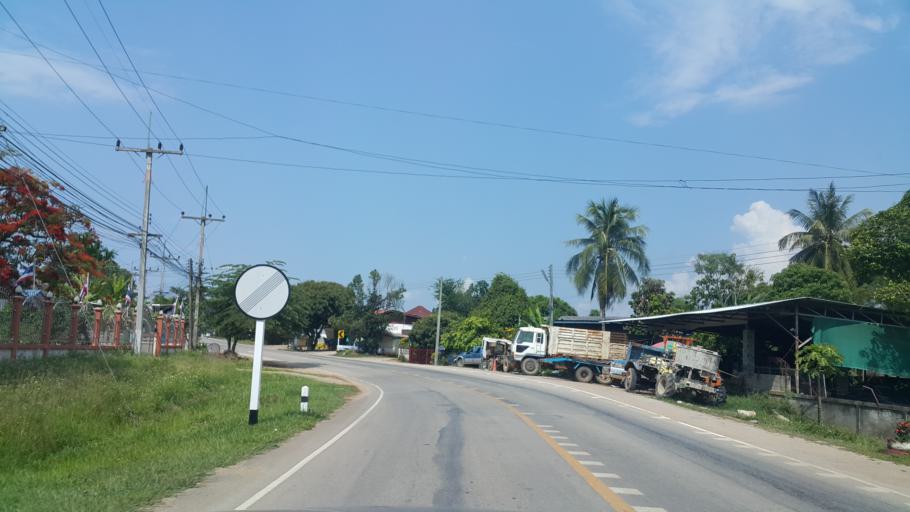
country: TH
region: Chiang Rai
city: Wiang Chiang Rung
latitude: 20.0145
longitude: 99.9283
